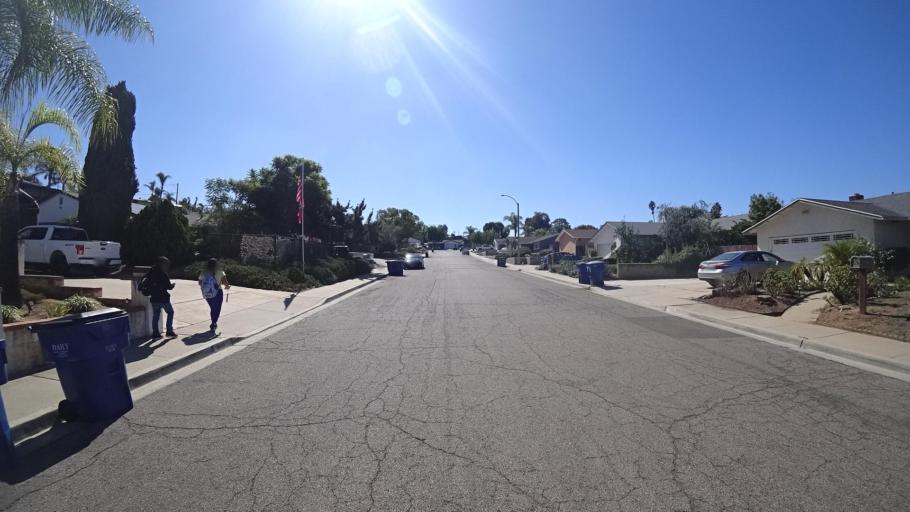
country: US
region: California
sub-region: San Diego County
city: Winter Gardens
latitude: 32.8186
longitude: -116.9276
